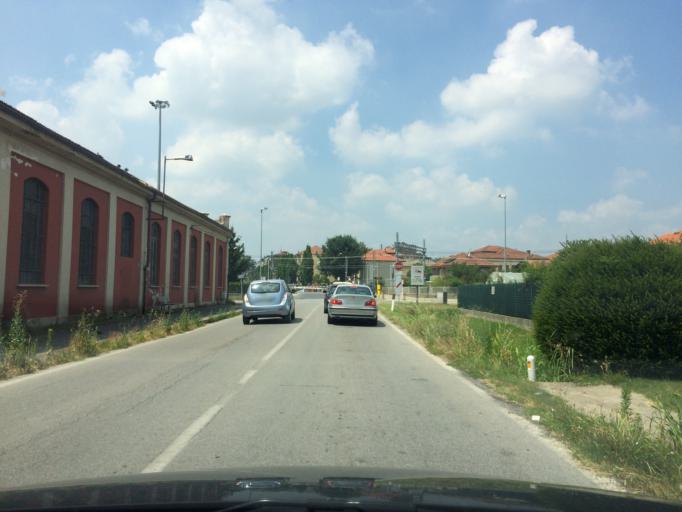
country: IT
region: Piedmont
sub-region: Provincia di Cuneo
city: Caramagna Piemonte
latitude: 44.7748
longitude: 7.7113
